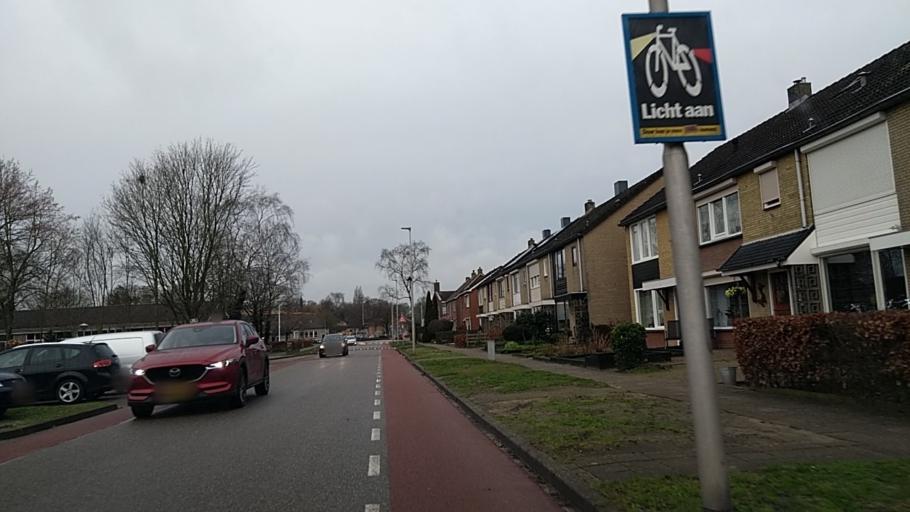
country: NL
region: Overijssel
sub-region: Gemeente Zwartewaterland
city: Hasselt
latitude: 52.5891
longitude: 6.1031
